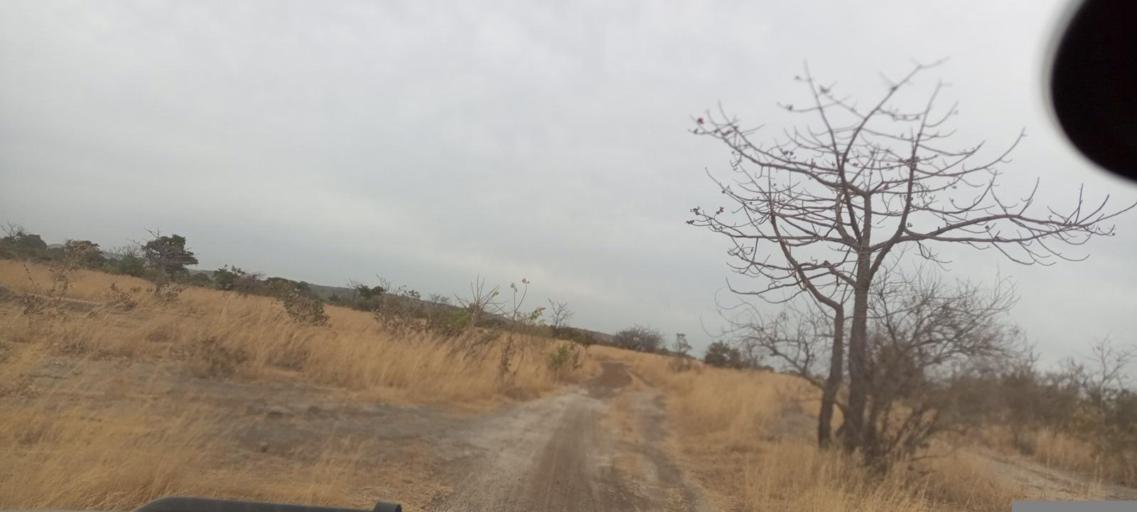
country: ML
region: Koulikoro
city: Kati
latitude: 12.7713
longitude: -8.3796
